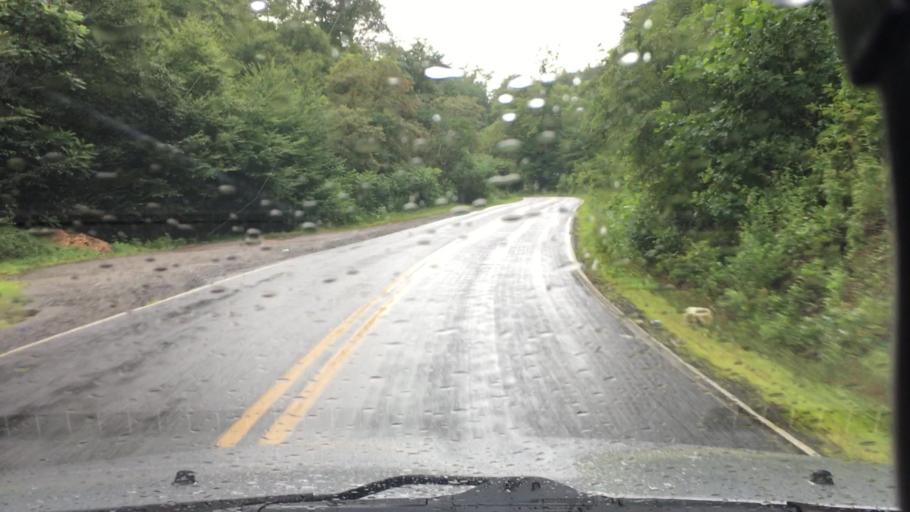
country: US
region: North Carolina
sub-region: Madison County
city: Mars Hill
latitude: 35.9118
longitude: -82.4891
